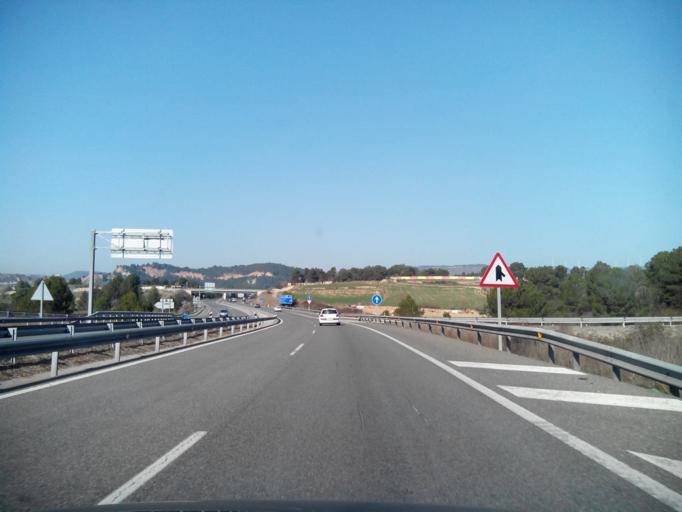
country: ES
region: Catalonia
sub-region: Provincia de Barcelona
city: Odena
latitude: 41.5936
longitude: 1.6491
